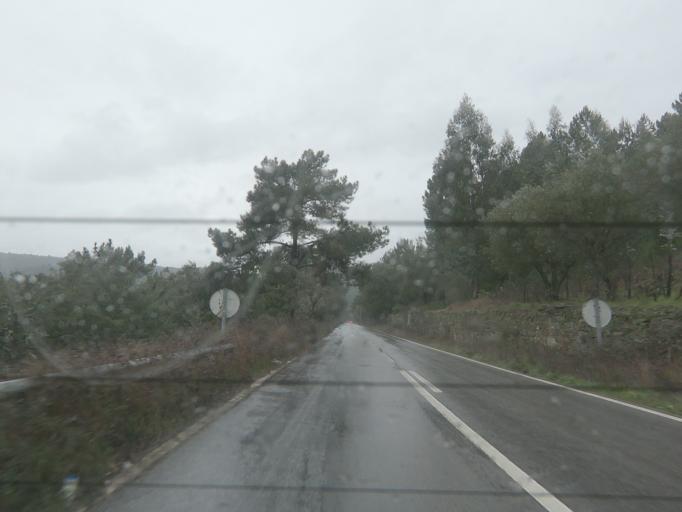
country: PT
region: Vila Real
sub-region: Sabrosa
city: Vilela
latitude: 41.2452
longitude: -7.6824
